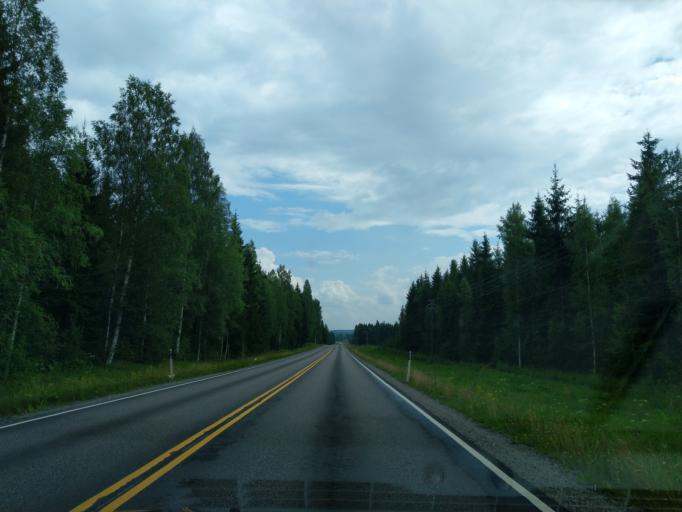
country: FI
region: South Karelia
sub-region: Imatra
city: Parikkala
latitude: 61.6145
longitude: 29.4497
